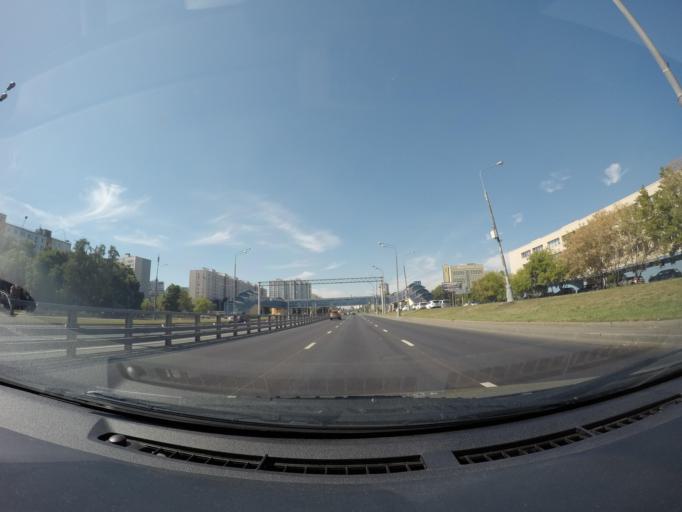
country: RU
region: Moscow
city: Veshnyaki
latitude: 55.7109
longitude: 37.8217
